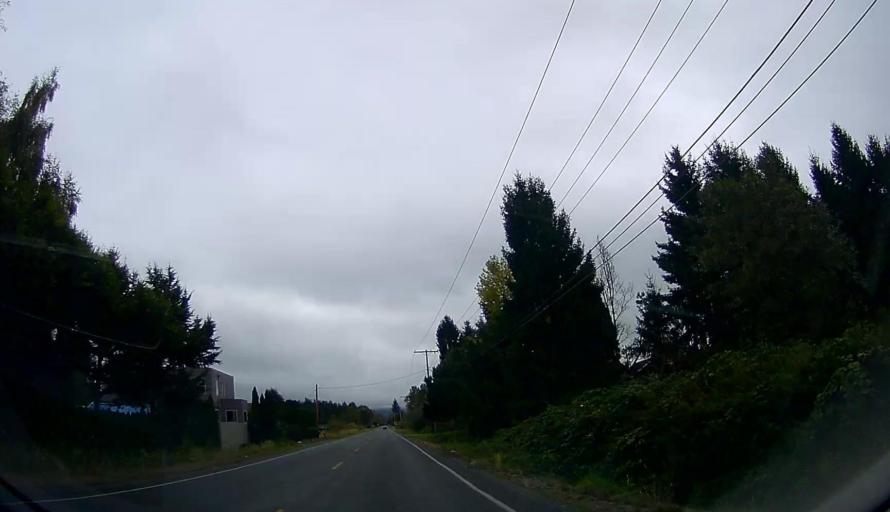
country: US
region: Washington
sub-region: Skagit County
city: Sedro-Woolley
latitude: 48.5124
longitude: -122.1943
